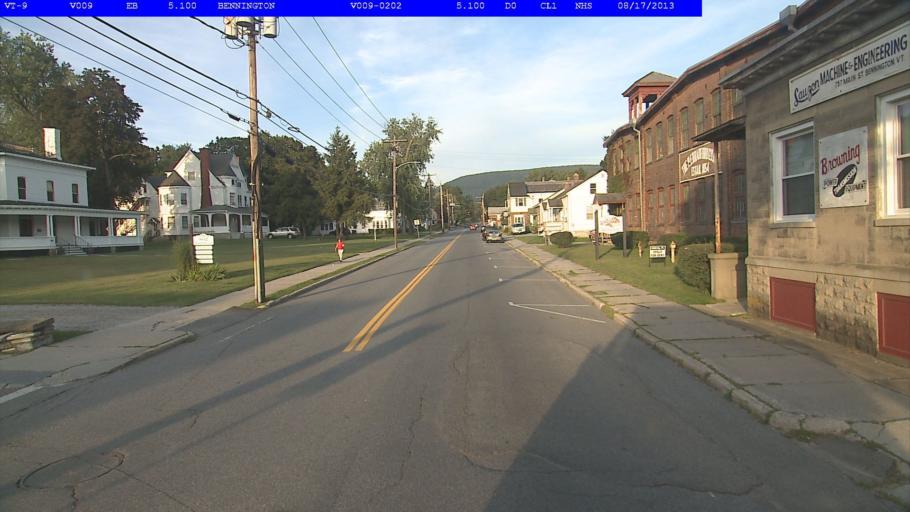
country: US
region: Vermont
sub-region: Bennington County
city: Bennington
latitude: 42.8792
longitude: -73.1836
